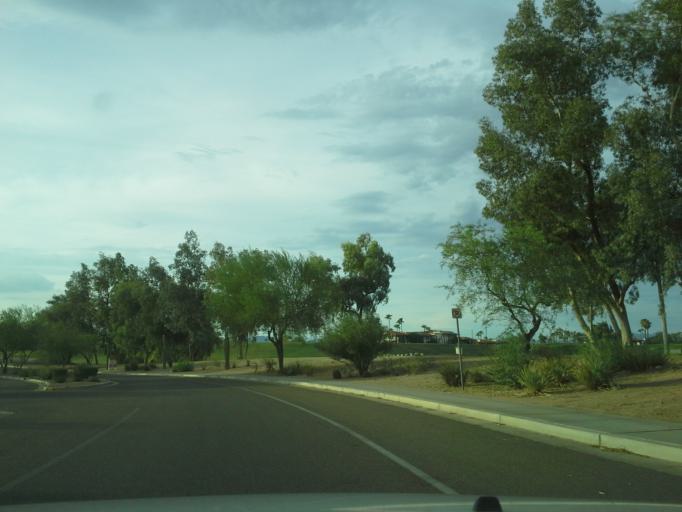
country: US
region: Arizona
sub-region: Maricopa County
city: Guadalupe
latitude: 33.3695
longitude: -111.9707
